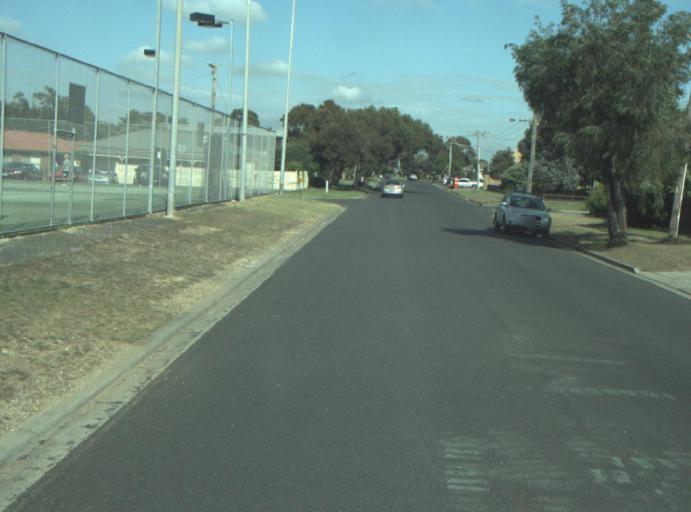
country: AU
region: Victoria
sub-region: Greater Geelong
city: Leopold
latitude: -38.2828
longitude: 144.5224
